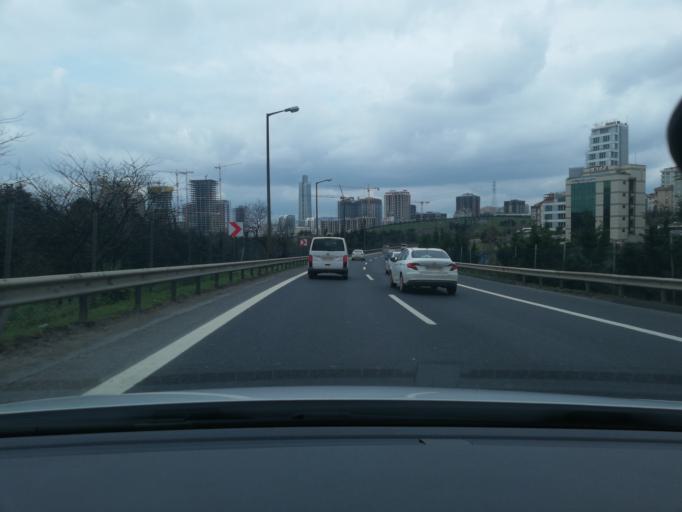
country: TR
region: Istanbul
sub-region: Atasehir
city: Atasehir
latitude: 40.9977
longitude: 29.1231
